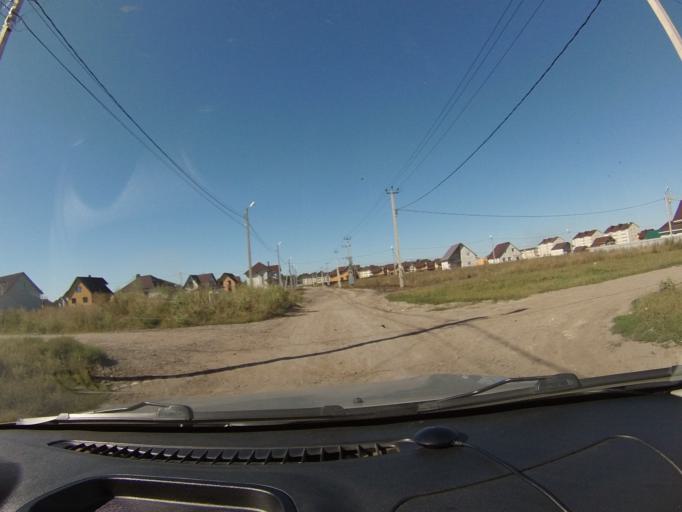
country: RU
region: Tambov
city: Komsomolets
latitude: 52.7804
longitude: 41.3694
